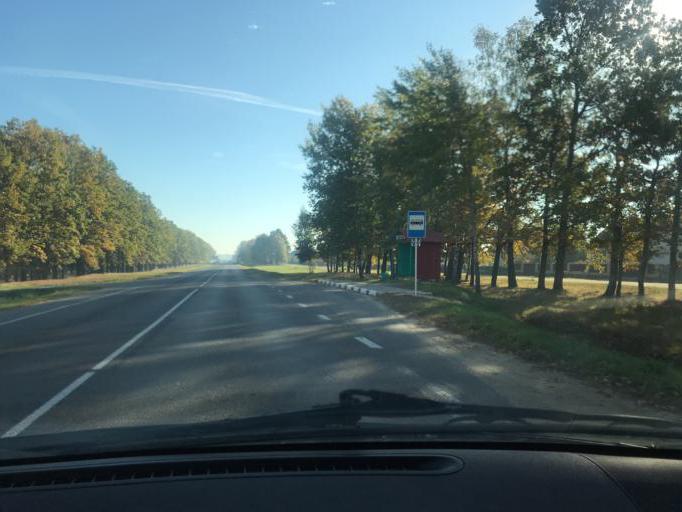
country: BY
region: Brest
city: Ivanava
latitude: 52.1438
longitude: 25.5061
